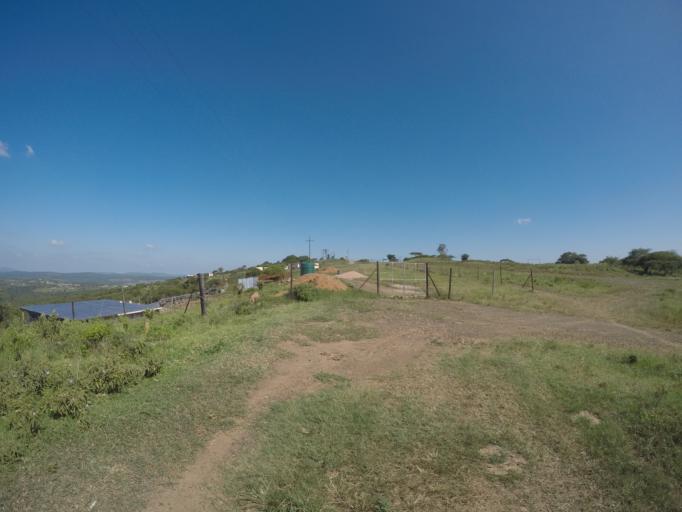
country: ZA
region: KwaZulu-Natal
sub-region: uThungulu District Municipality
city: Empangeni
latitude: -28.5634
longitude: 31.7085
